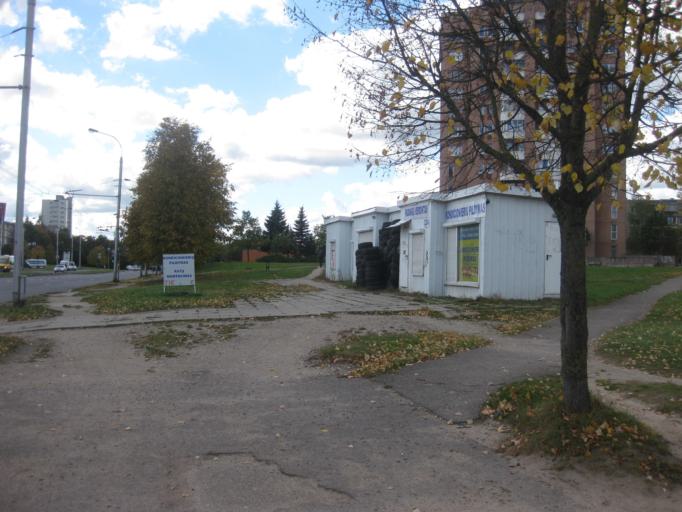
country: LT
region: Kauno apskritis
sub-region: Kaunas
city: Eiguliai
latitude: 54.9297
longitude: 23.9304
